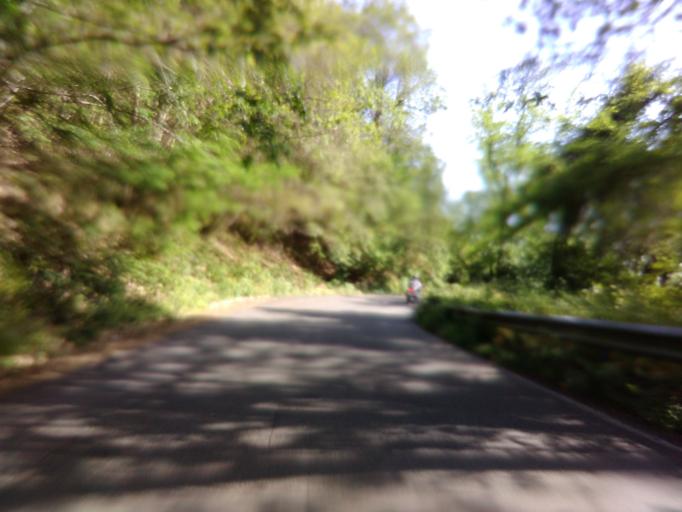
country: IT
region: Tuscany
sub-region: Provincia di Massa-Carrara
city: Fosdinovo
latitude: 44.1196
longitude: 10.0652
